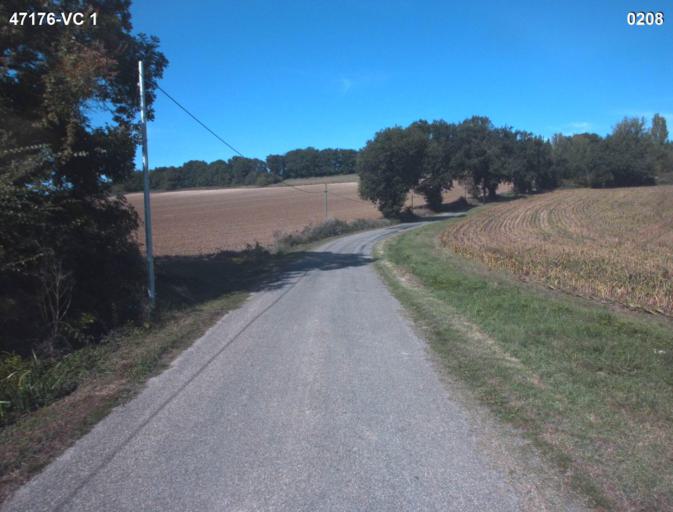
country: FR
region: Aquitaine
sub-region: Departement du Lot-et-Garonne
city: Lavardac
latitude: 44.1949
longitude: 0.2926
